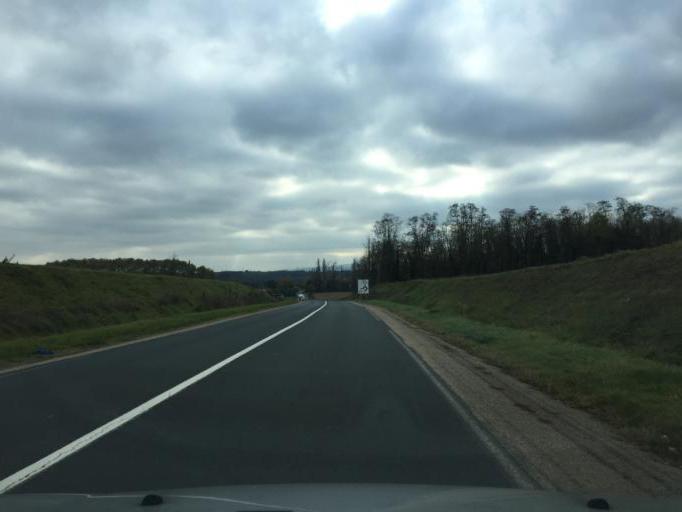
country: FR
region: Rhone-Alpes
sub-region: Departement de l'Ain
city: Sainte-Euphemie
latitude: 45.9849
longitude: 4.7971
